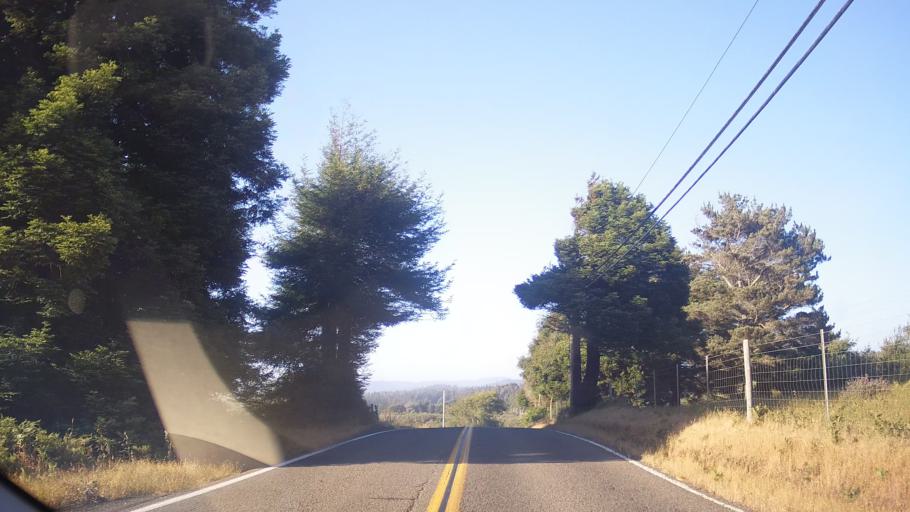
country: US
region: California
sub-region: Mendocino County
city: Fort Bragg
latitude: 39.5026
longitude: -123.7717
